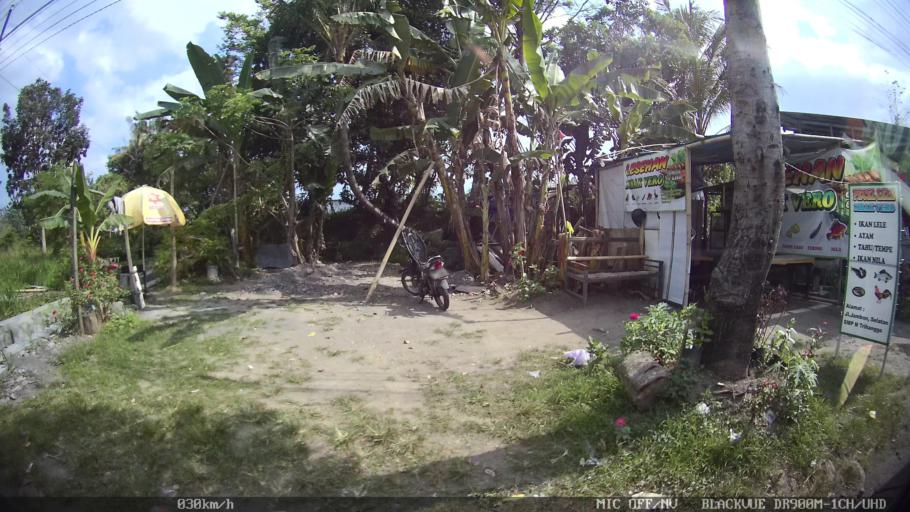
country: ID
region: Daerah Istimewa Yogyakarta
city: Yogyakarta
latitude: -7.7626
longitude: 110.3465
